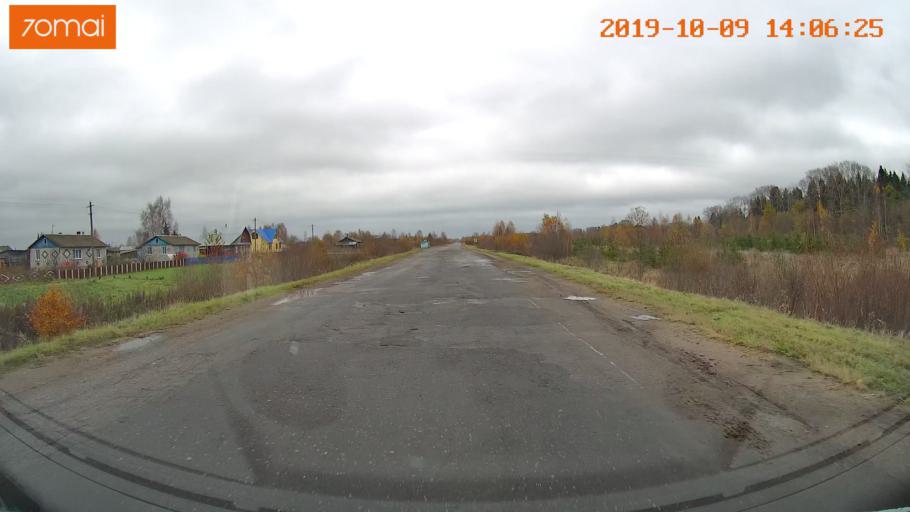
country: RU
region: Kostroma
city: Buy
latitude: 58.4648
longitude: 41.4108
